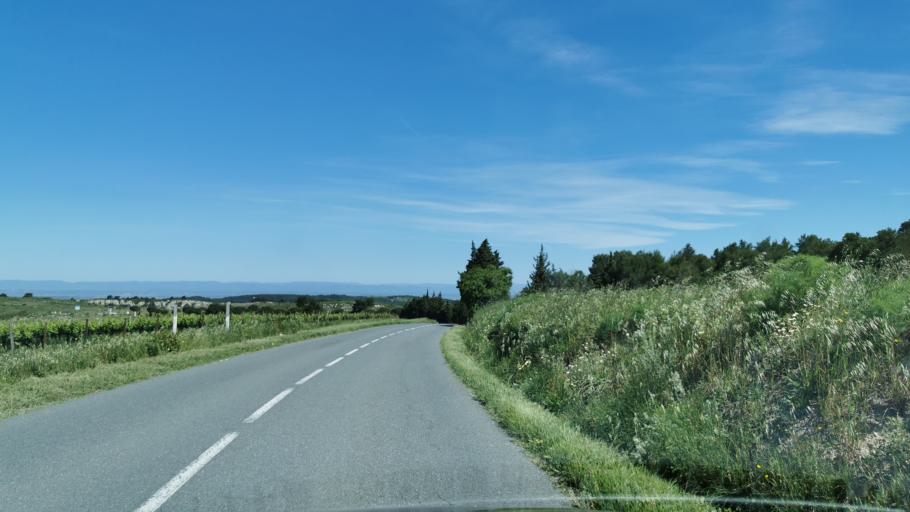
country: FR
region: Languedoc-Roussillon
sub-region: Departement de l'Aude
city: Armissan
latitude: 43.1726
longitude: 3.1121
